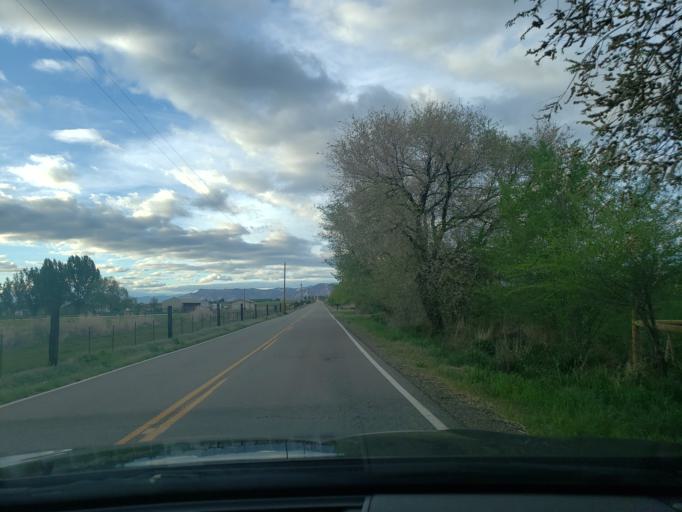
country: US
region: Colorado
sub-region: Mesa County
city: Fruita
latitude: 39.2157
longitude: -108.7197
